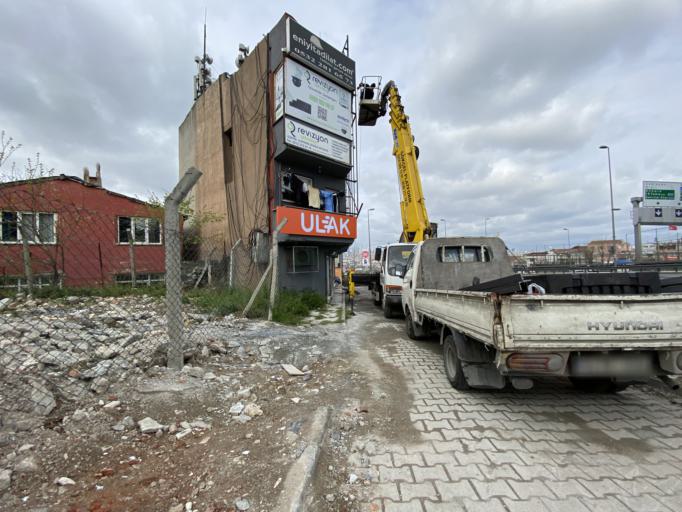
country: TR
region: Istanbul
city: Istanbul
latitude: 41.0363
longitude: 28.9335
